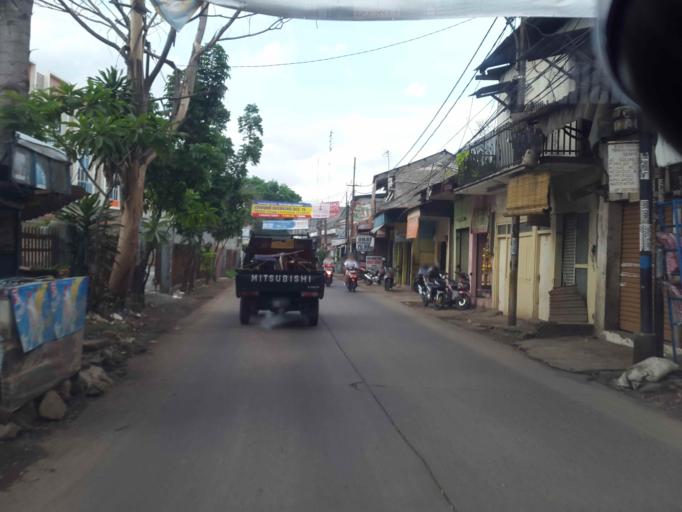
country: ID
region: West Java
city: Bekasi
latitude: -6.2982
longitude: 106.9233
